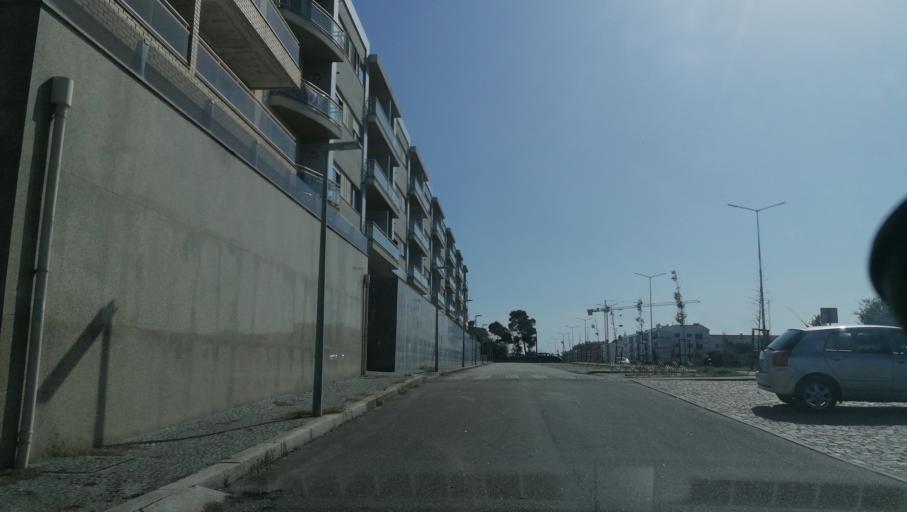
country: PT
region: Aveiro
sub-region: Espinho
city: Espinho
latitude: 41.0103
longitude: -8.6338
